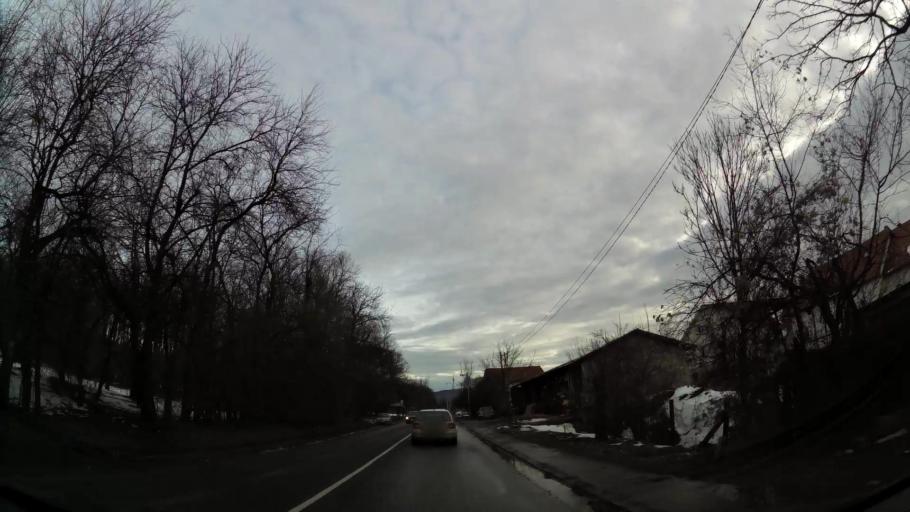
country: RS
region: Central Serbia
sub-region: Belgrade
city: Rakovica
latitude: 44.7301
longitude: 20.4837
